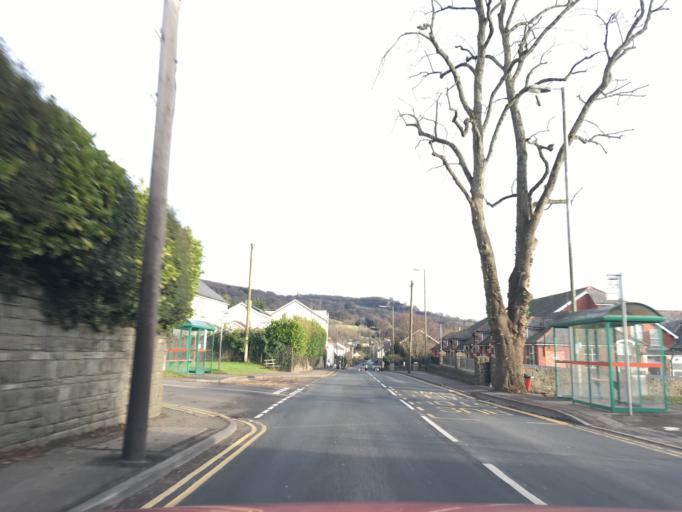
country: GB
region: Wales
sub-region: Caerphilly County Borough
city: Machen
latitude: 51.5961
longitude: -3.1438
